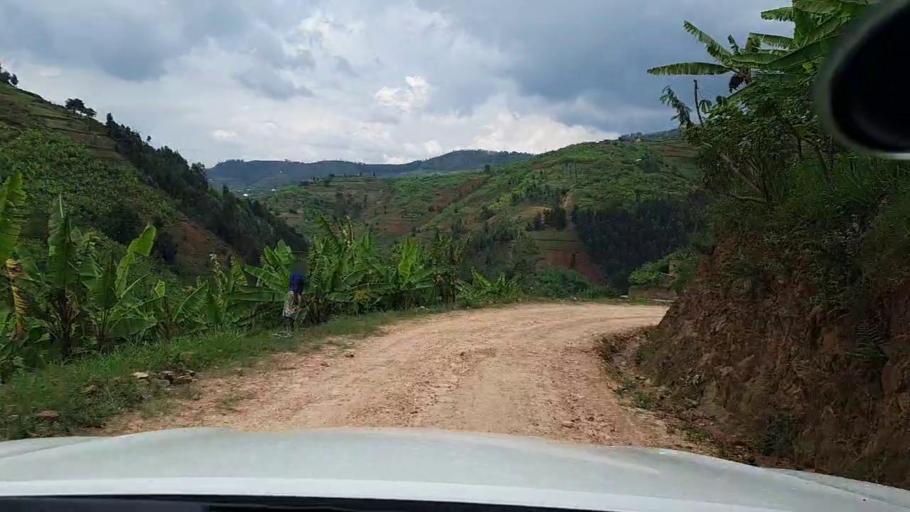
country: RW
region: Western Province
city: Kibuye
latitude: -2.1292
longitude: 29.4262
